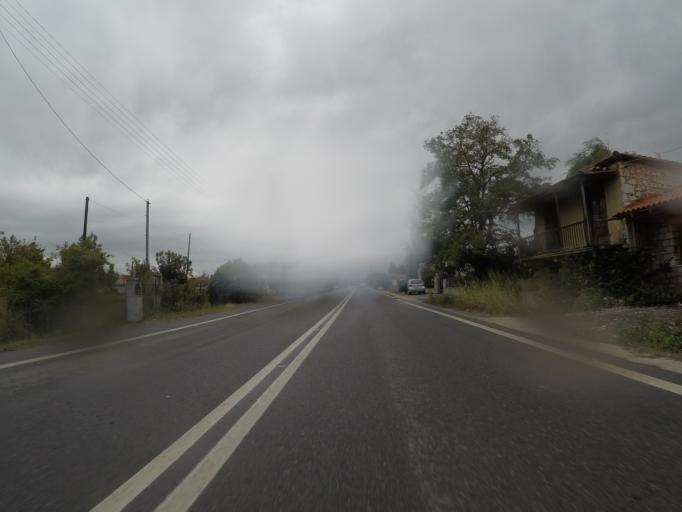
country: GR
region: Peloponnese
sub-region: Nomos Arkadias
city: Tripoli
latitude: 37.5535
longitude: 22.3998
